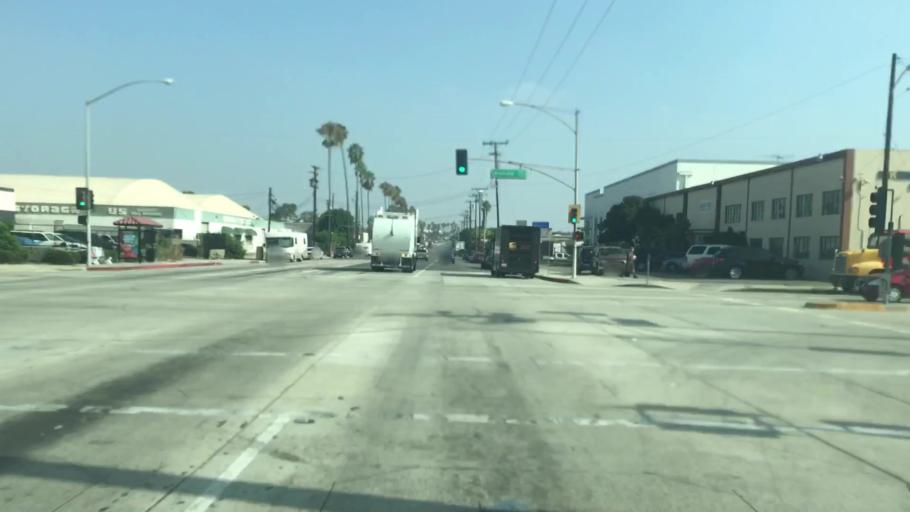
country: US
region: California
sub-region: Los Angeles County
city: West Rancho Dominguez
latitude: 33.8851
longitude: -118.2783
